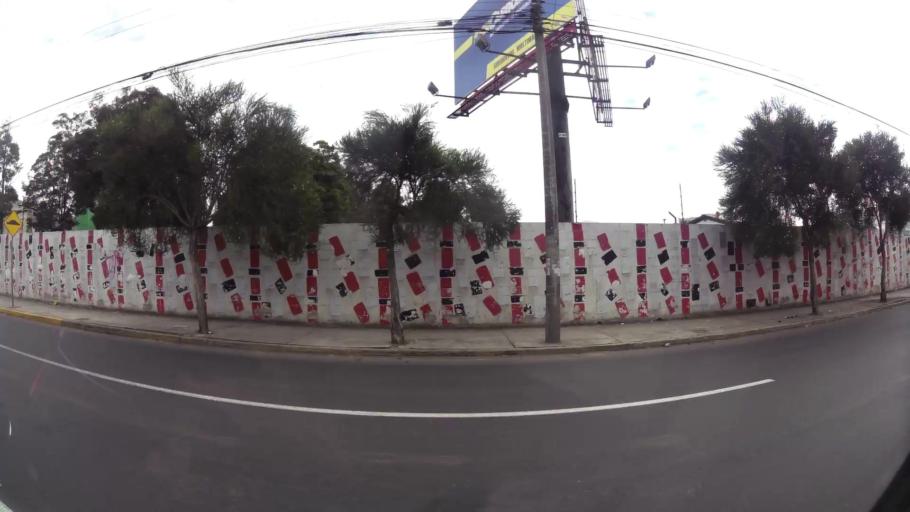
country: EC
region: Pichincha
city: Quito
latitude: -0.1639
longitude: -78.4646
